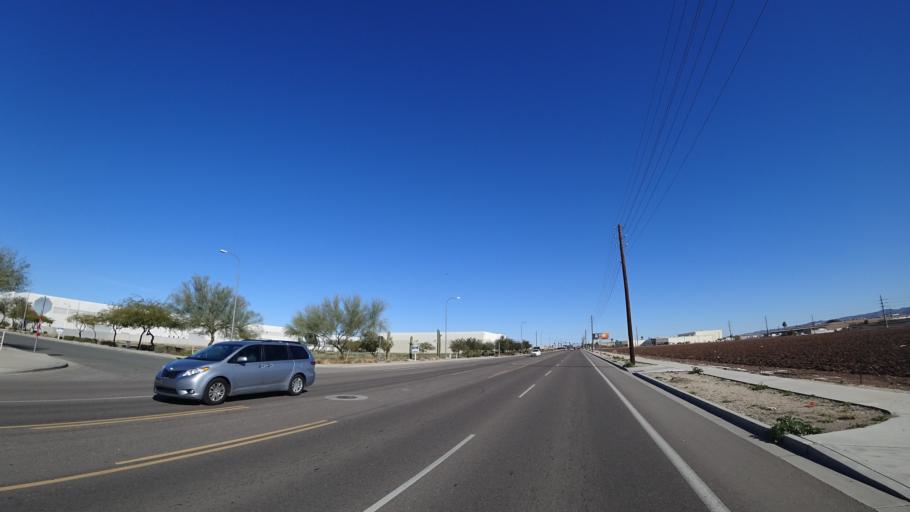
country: US
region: Arizona
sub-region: Maricopa County
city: Laveen
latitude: 33.4224
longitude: -112.1561
